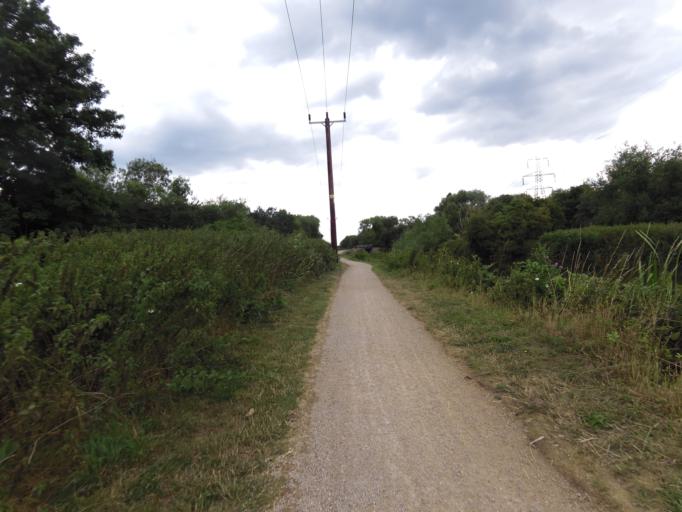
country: GB
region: England
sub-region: Hertfordshire
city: Cheshunt
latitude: 51.7207
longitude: -0.0146
